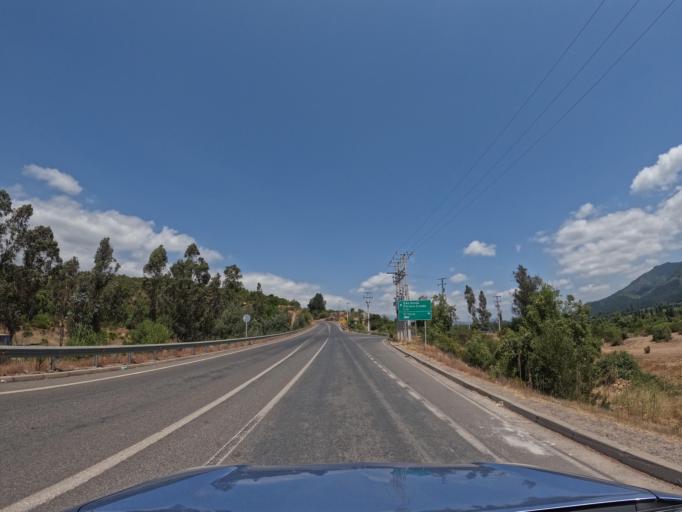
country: CL
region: Maule
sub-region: Provincia de Curico
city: Molina
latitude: -35.1797
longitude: -71.1190
